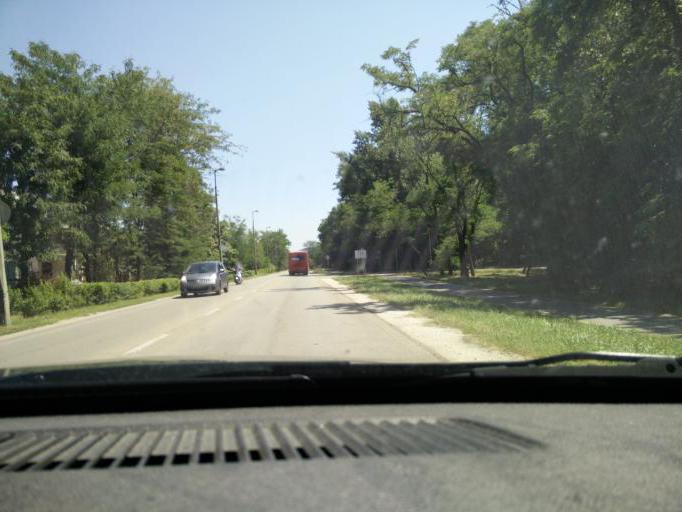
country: HU
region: Komarom-Esztergom
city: Baj
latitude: 47.6417
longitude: 18.3419
